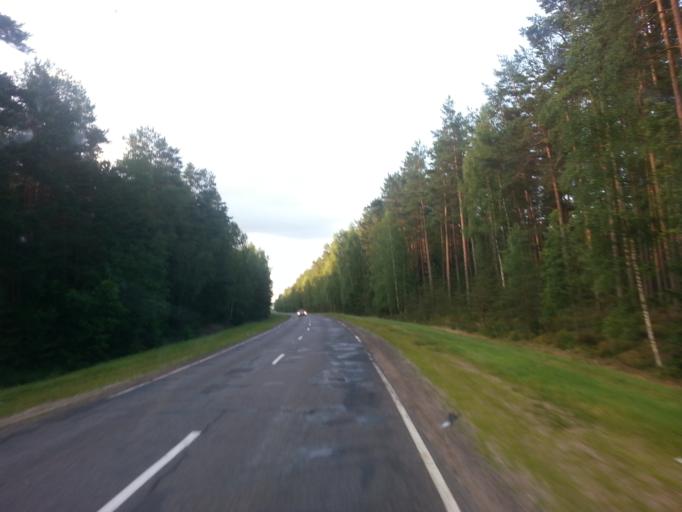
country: BY
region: Minsk
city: Il'ya
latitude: 54.4897
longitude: 27.2387
